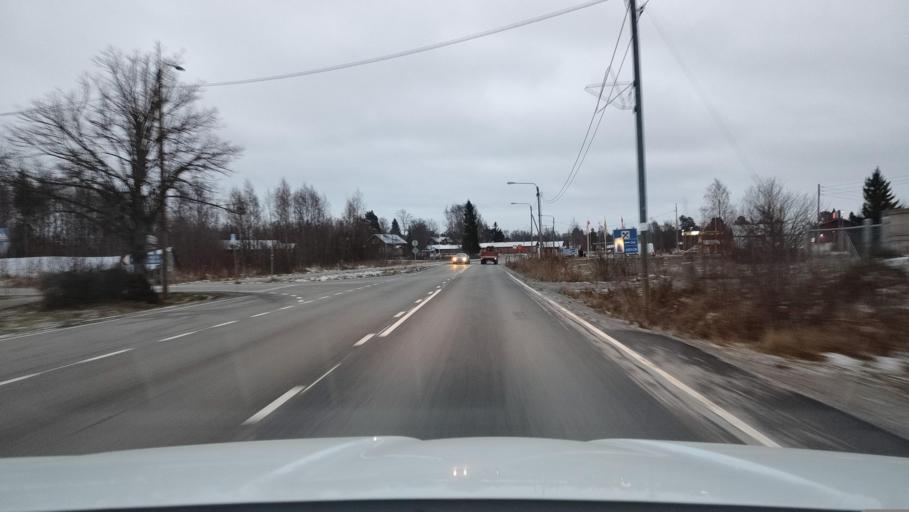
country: FI
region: Ostrobothnia
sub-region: Vaasa
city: Replot
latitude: 63.2331
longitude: 21.4065
